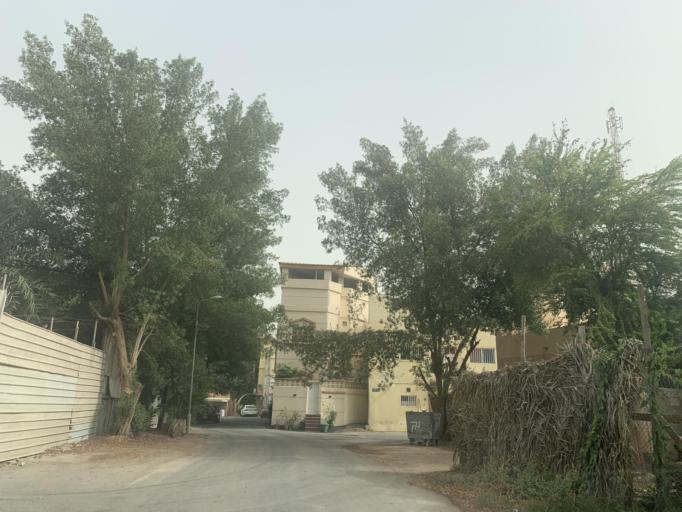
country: BH
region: Manama
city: Jidd Hafs
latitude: 26.2235
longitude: 50.5579
